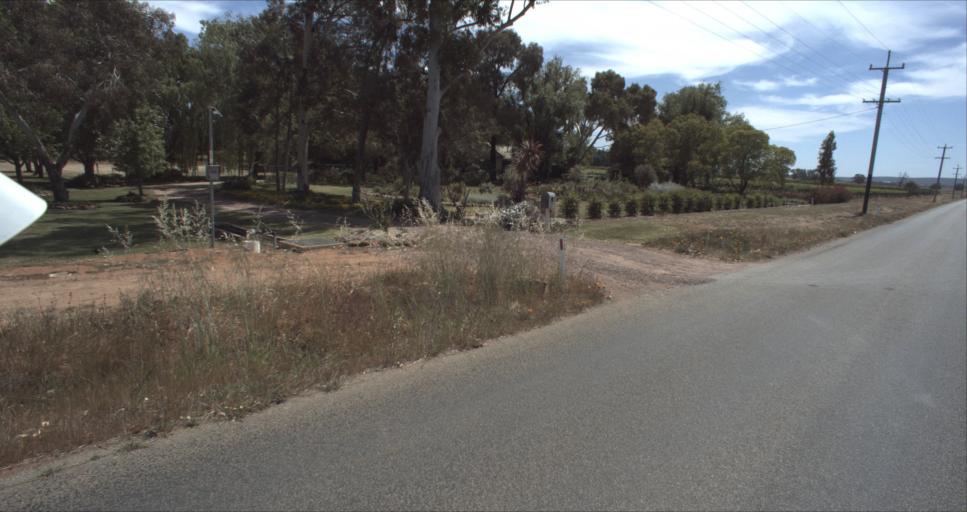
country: AU
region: New South Wales
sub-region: Leeton
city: Leeton
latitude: -34.5622
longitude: 146.4526
